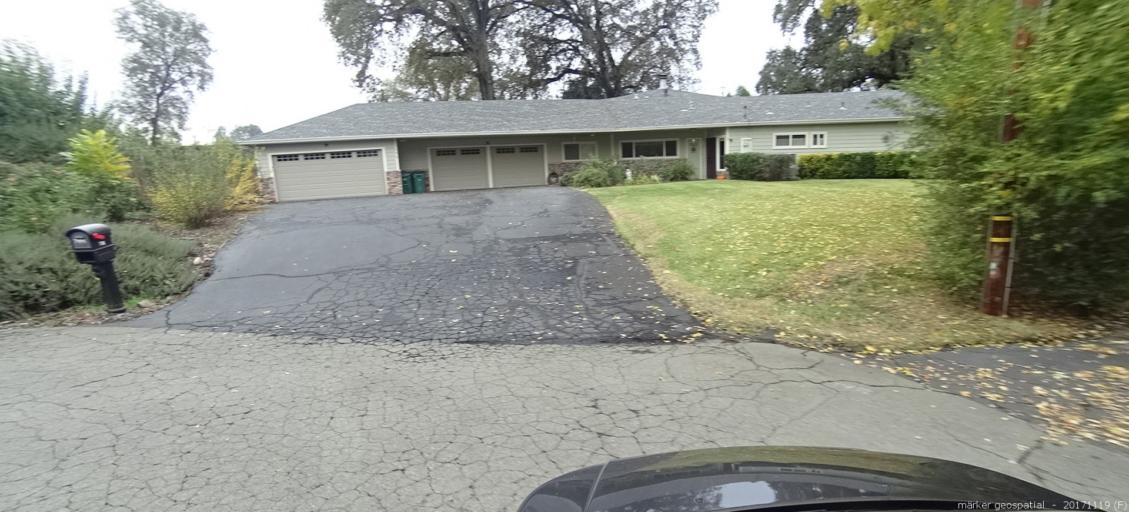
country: US
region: California
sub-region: Shasta County
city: Anderson
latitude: 40.4931
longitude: -122.3504
